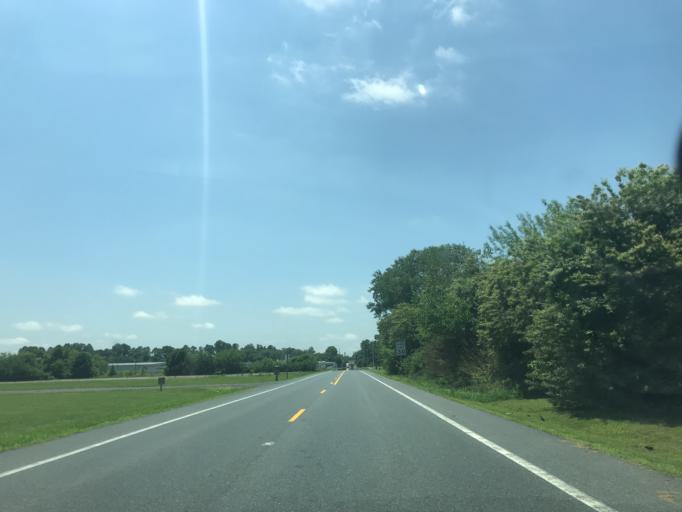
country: US
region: Maryland
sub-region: Dorchester County
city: Hurlock
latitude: 38.6325
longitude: -75.8470
